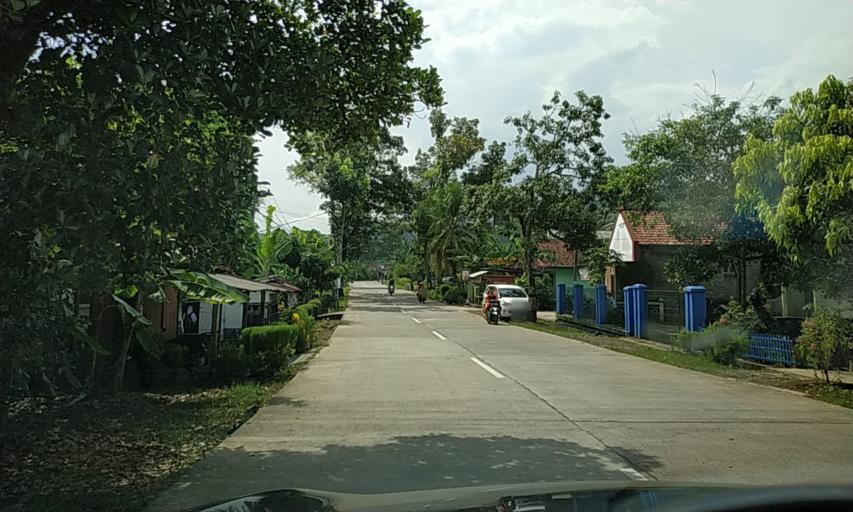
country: ID
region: Central Java
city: Winangun
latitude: -7.3443
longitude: 108.7082
